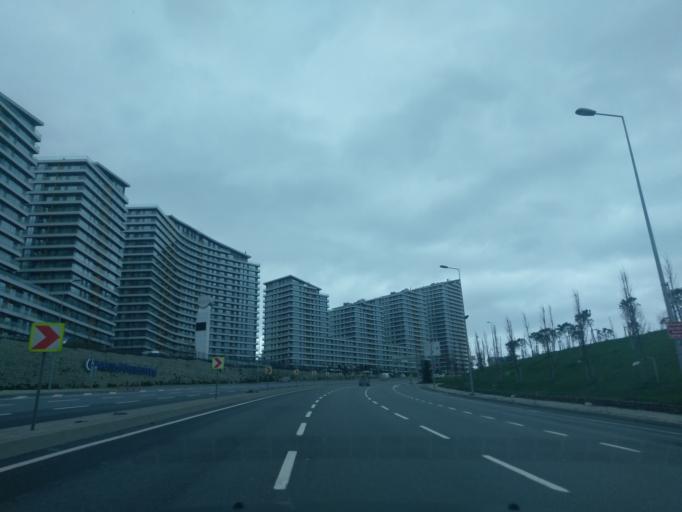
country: TR
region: Istanbul
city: Mahmutbey
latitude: 41.0652
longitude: 28.8443
